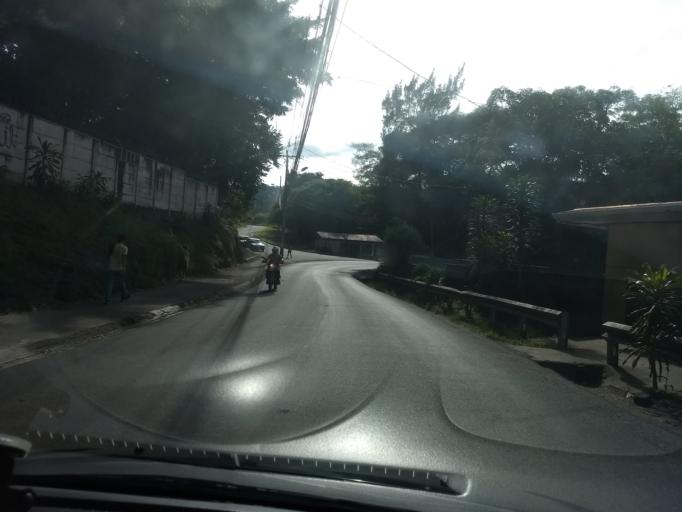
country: CR
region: San Jose
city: Santa Ana
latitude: 9.9469
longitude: -84.1883
